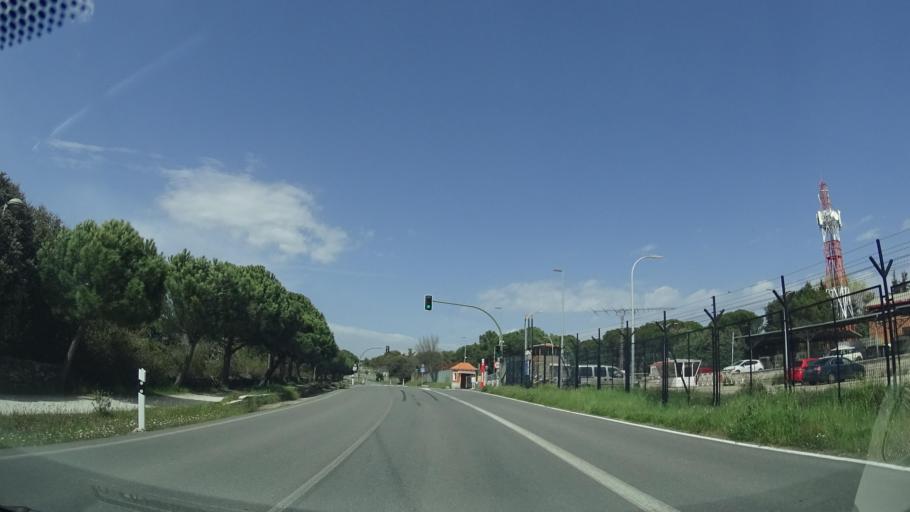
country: ES
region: Madrid
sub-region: Provincia de Madrid
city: Colmenar Viejo
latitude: 40.6961
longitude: -3.7682
